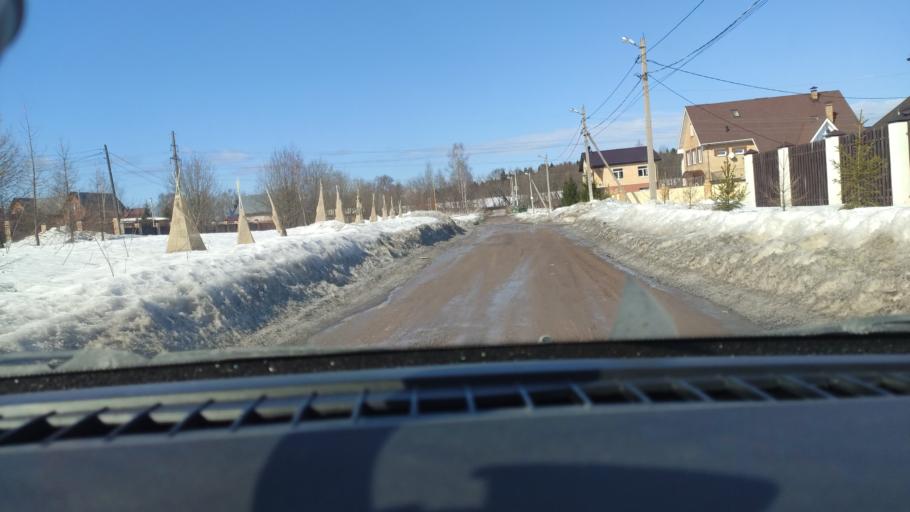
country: RU
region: Perm
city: Perm
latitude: 58.0379
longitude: 56.3948
